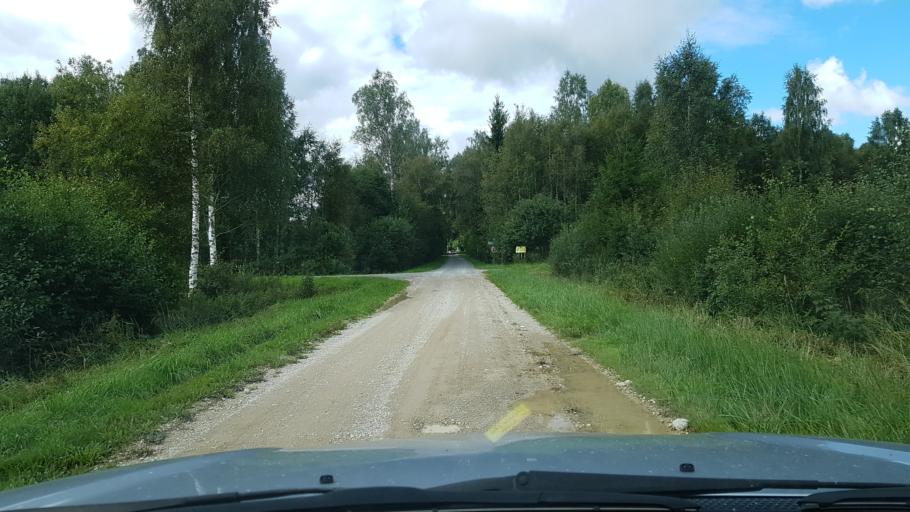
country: EE
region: Harju
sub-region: Raasiku vald
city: Arukula
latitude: 59.3021
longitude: 25.0590
